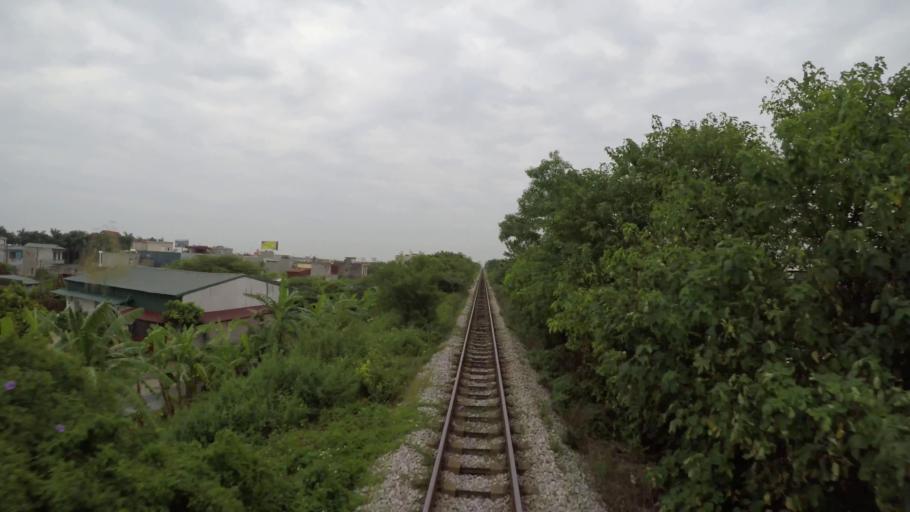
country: VN
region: Hai Duong
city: Thanh Pho Hai Duong
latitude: 20.9507
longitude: 106.3621
